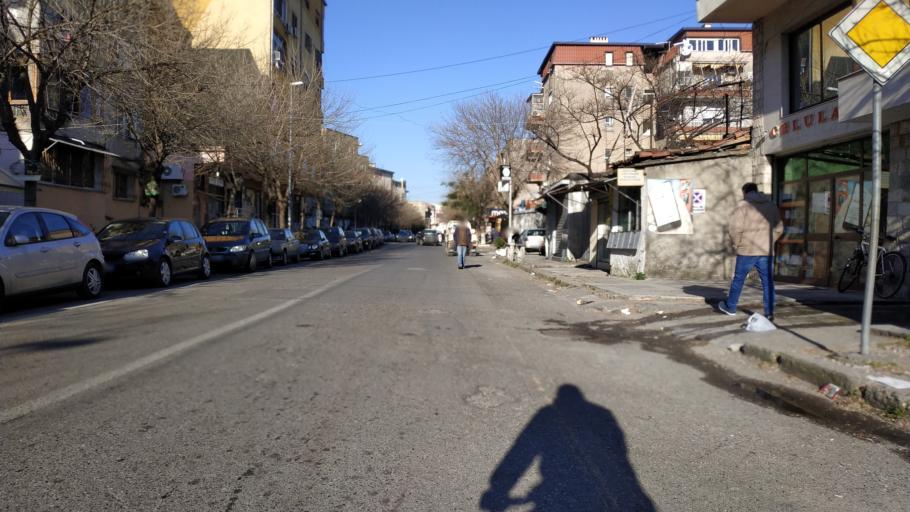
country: AL
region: Shkoder
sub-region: Rrethi i Shkodres
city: Shkoder
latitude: 42.0631
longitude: 19.5106
